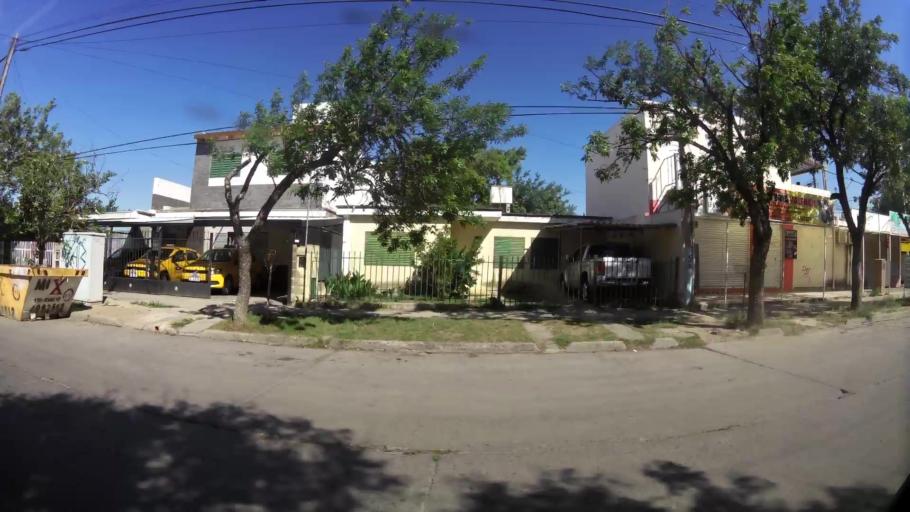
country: AR
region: Cordoba
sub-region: Departamento de Capital
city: Cordoba
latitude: -31.3643
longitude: -64.1713
